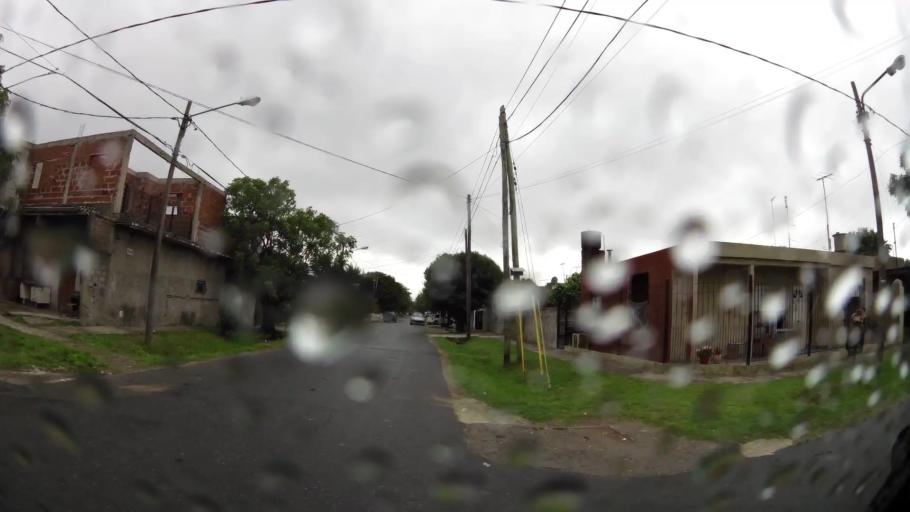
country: AR
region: Buenos Aires
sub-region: Partido de Quilmes
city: Quilmes
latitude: -34.7805
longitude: -58.2296
